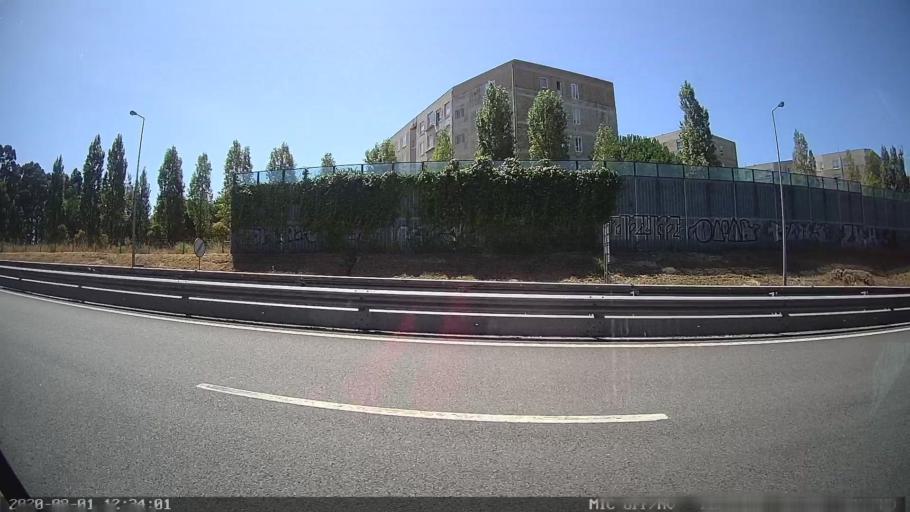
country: PT
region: Porto
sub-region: Matosinhos
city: Santa Cruz do Bispo
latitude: 41.2327
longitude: -8.6925
